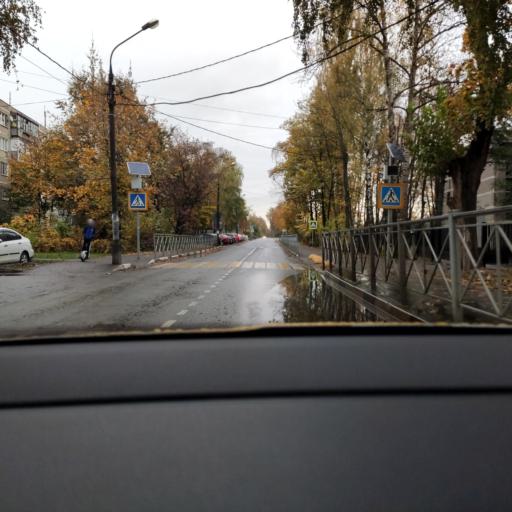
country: RU
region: Moskovskaya
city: Ivanteyevka
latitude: 55.9703
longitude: 37.9455
